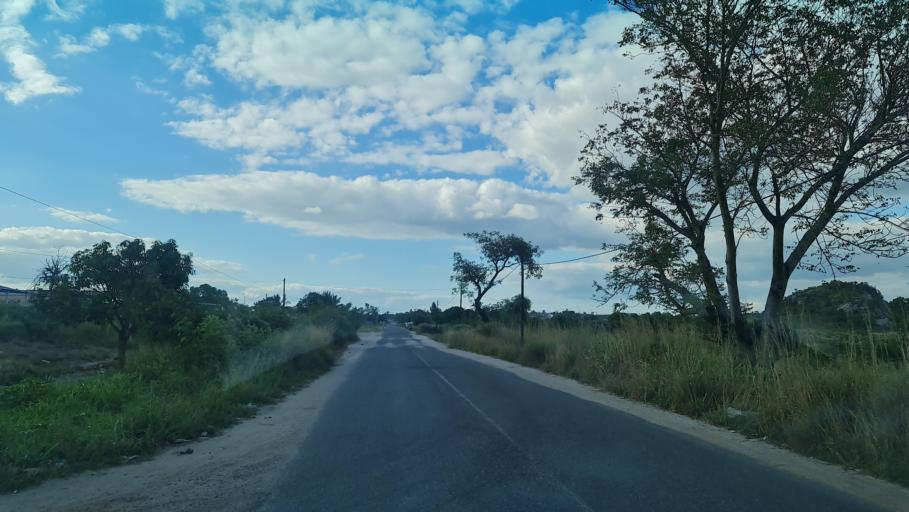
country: MZ
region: Manica
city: Chimoio
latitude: -19.2183
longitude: 33.9222
